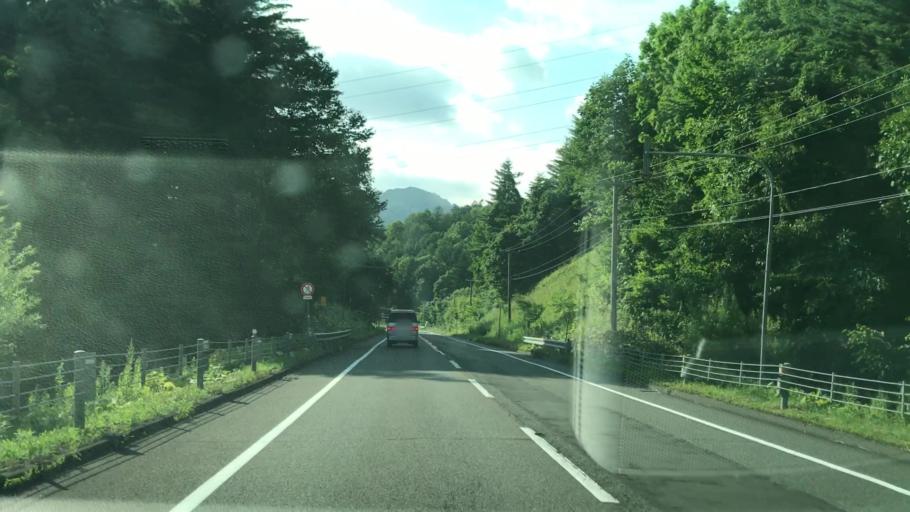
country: JP
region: Hokkaido
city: Shimo-furano
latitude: 42.8895
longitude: 142.1978
